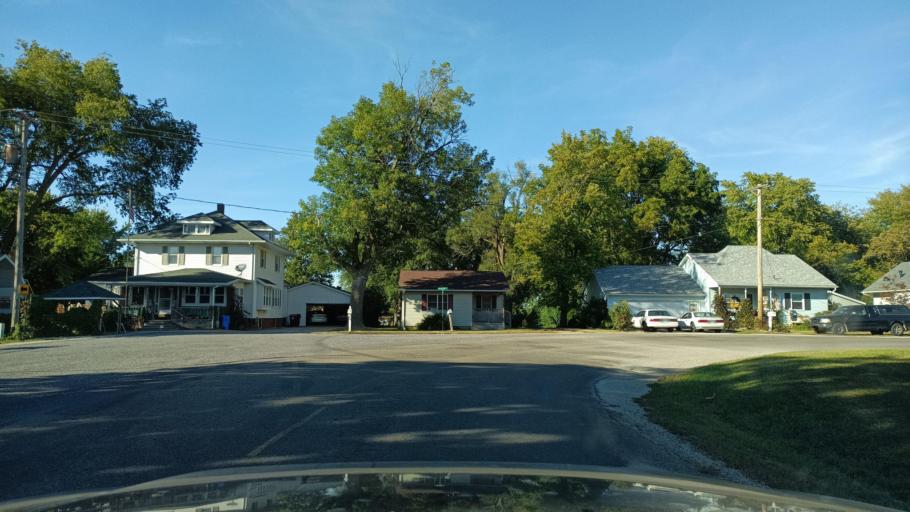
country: US
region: Illinois
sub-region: De Witt County
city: Clinton
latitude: 40.2240
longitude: -88.9595
